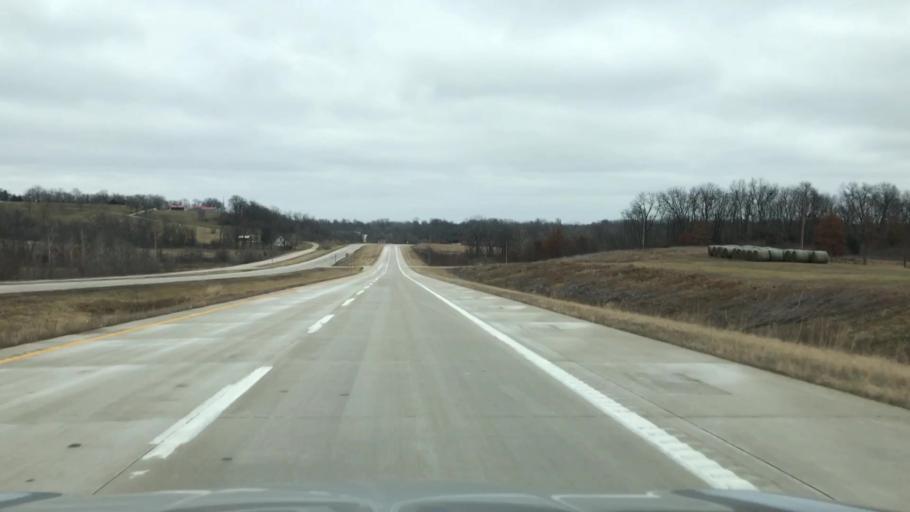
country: US
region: Missouri
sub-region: Livingston County
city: Chillicothe
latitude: 39.7397
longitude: -93.6511
